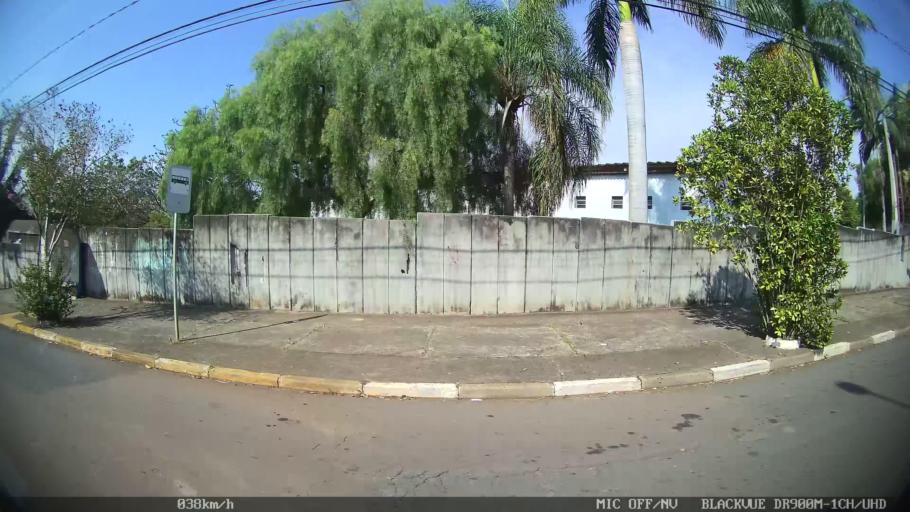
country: BR
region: Sao Paulo
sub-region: Paulinia
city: Paulinia
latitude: -22.7703
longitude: -47.1581
